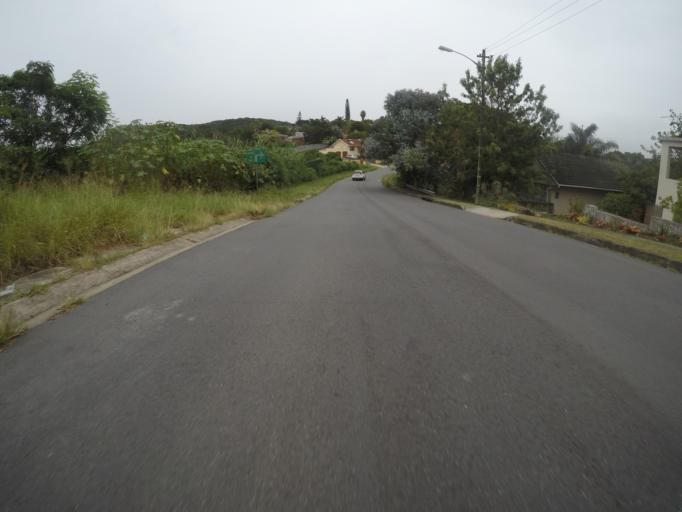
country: ZA
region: Eastern Cape
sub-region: Buffalo City Metropolitan Municipality
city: East London
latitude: -32.9731
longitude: 27.9211
